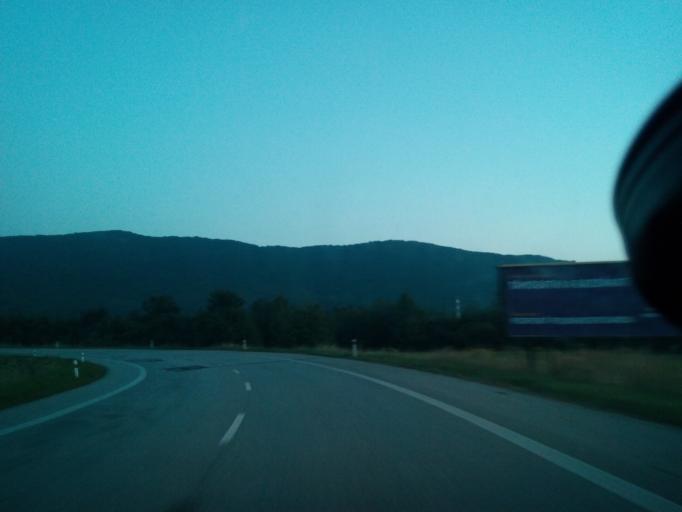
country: SK
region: Kosicky
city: Roznava
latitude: 48.6414
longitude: 20.5247
